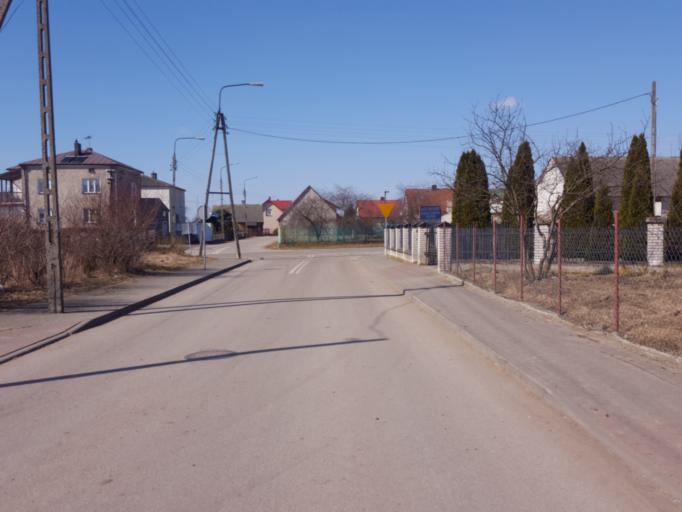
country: PL
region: Podlasie
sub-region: Powiat kolnenski
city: Stawiski
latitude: 53.3772
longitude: 22.1511
